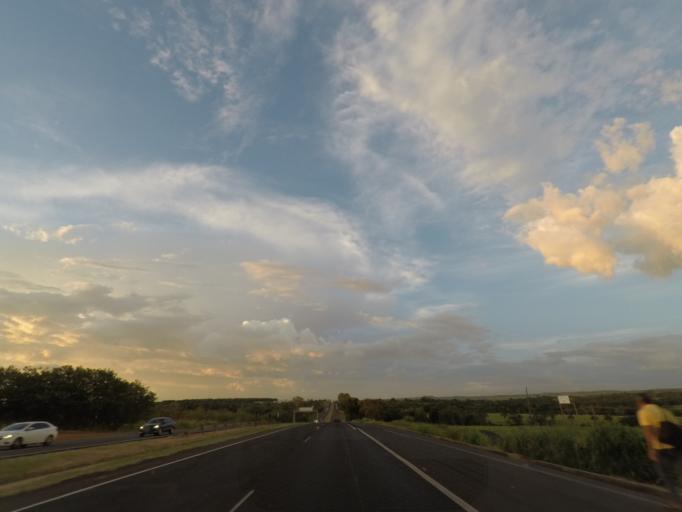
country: BR
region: Minas Gerais
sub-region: Uberaba
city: Uberaba
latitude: -19.6818
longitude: -47.9939
